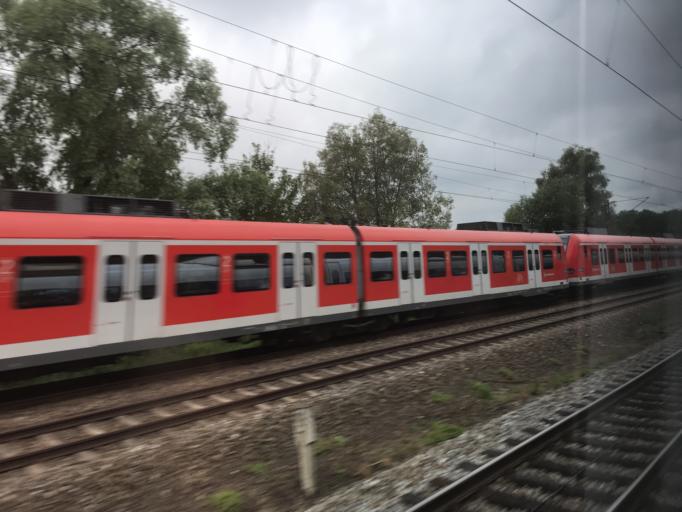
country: DE
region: Bavaria
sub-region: Upper Bavaria
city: Grobenzell
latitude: 48.2007
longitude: 11.3638
